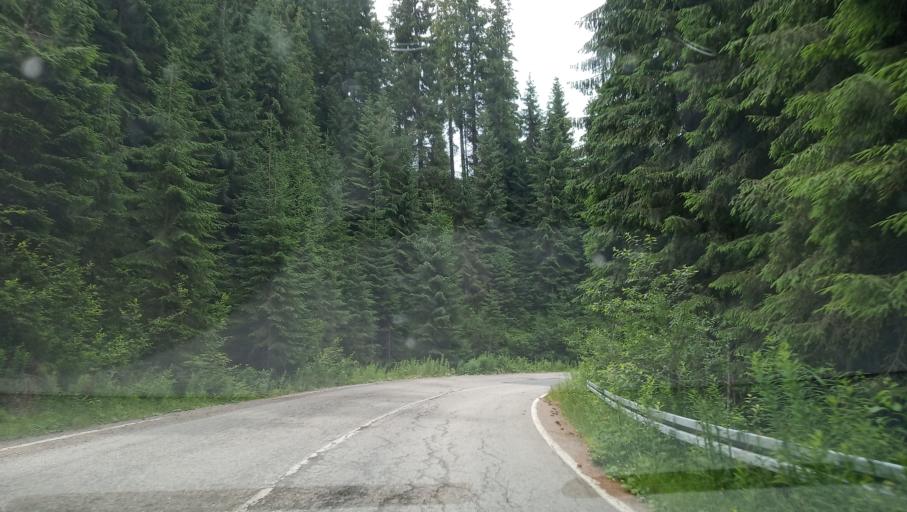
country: RO
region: Valcea
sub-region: Comuna Voineasa
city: Voineasa
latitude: 45.4212
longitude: 23.7403
